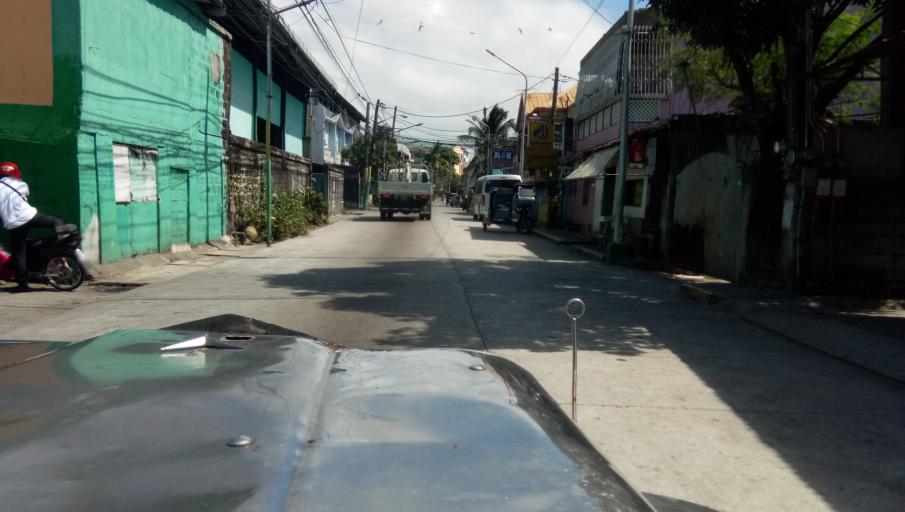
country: PH
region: Calabarzon
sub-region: Province of Cavite
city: Dasmarinas
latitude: 14.3283
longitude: 120.9334
